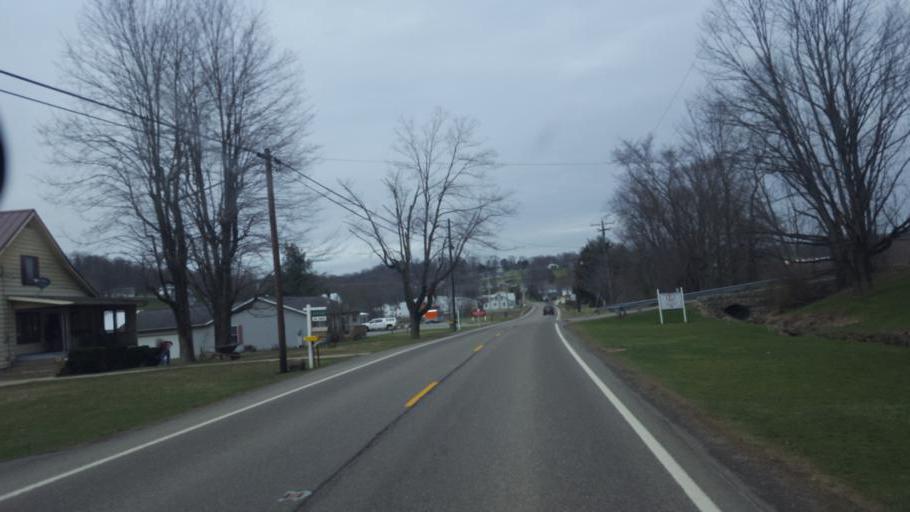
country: US
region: Ohio
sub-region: Tuscarawas County
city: Sugarcreek
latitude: 40.5874
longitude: -81.7066
